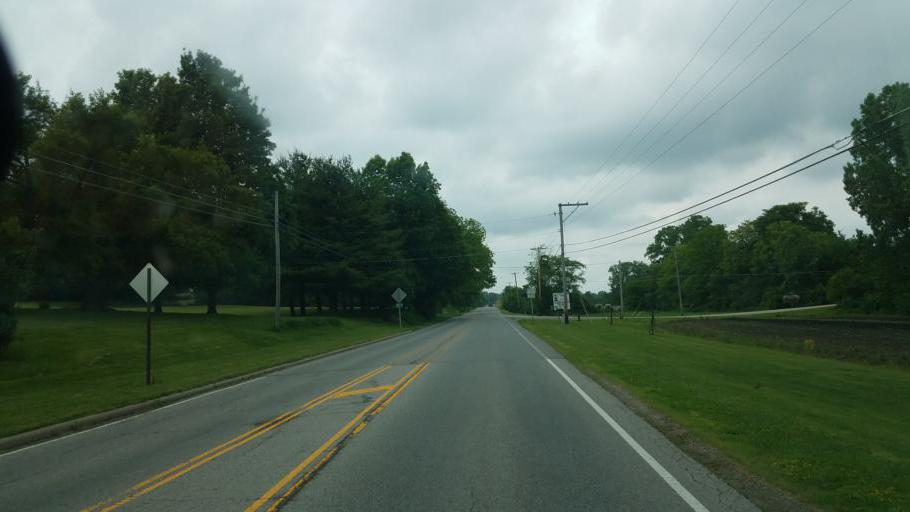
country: US
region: Ohio
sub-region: Delaware County
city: Delaware
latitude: 40.3154
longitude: -83.1180
